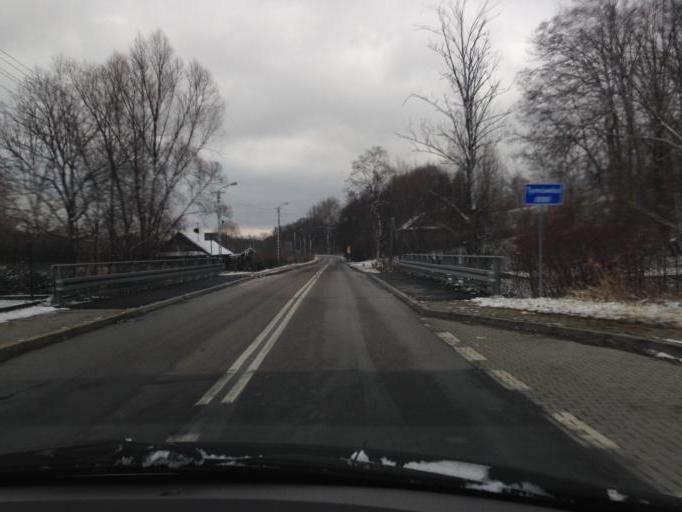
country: PL
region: Lesser Poland Voivodeship
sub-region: Powiat brzeski
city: Gnojnik
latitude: 49.8513
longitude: 20.6224
